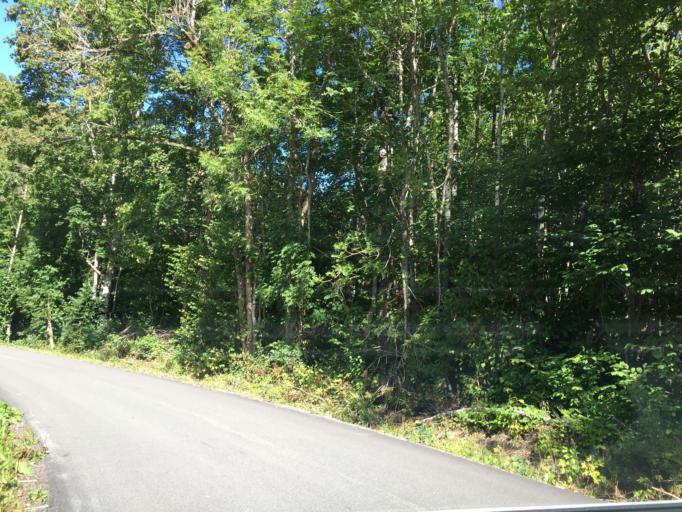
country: NO
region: Vestfold
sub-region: Hof
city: Hof
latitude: 59.4870
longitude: 10.1556
